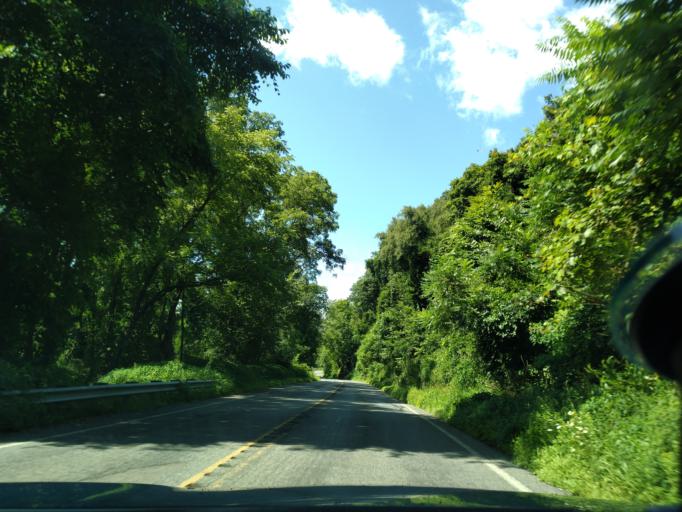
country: US
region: Pennsylvania
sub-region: Pike County
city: Pocono Ranch Lands
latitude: 41.1162
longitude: -74.9751
